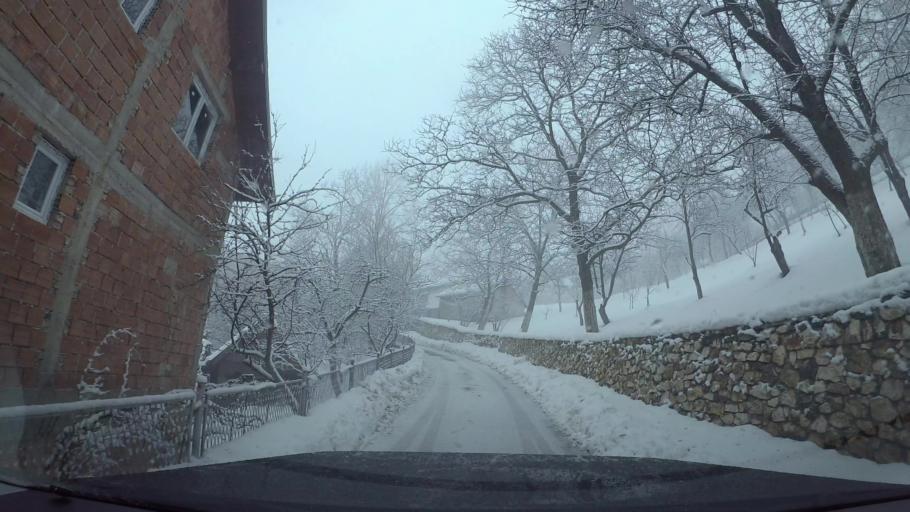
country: BA
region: Federation of Bosnia and Herzegovina
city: Kobilja Glava
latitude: 43.8497
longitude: 18.4429
